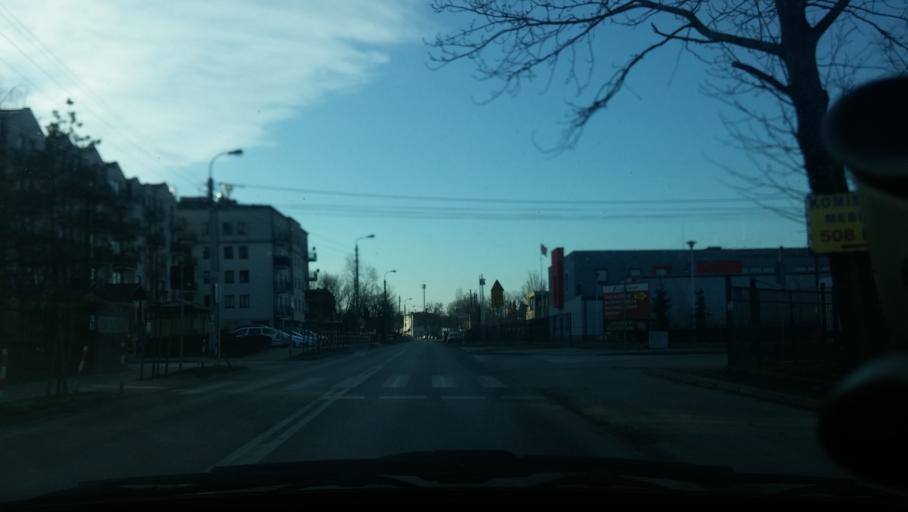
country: PL
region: Masovian Voivodeship
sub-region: Powiat piaseczynski
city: Piaseczno
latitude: 52.0702
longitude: 21.0164
